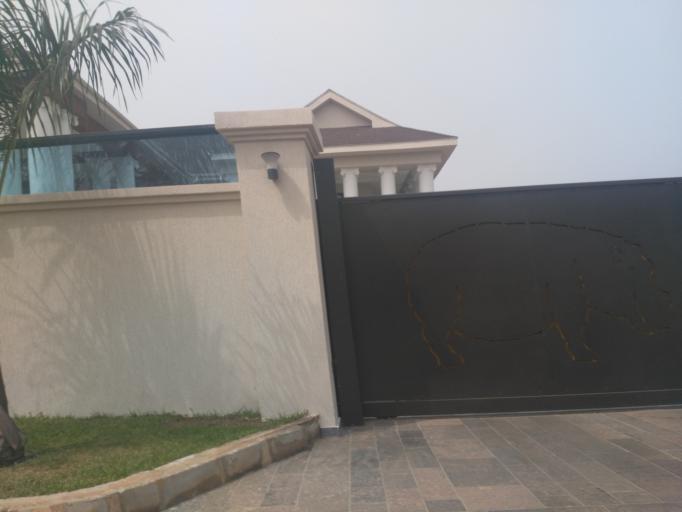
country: GH
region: Ashanti
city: Kumasi
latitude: 6.6873
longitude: -1.6327
